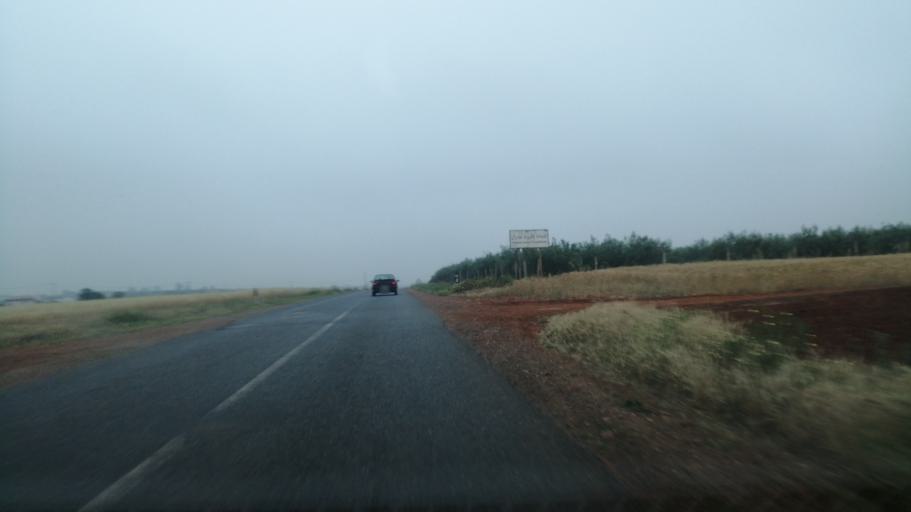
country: MA
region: Rabat-Sale-Zemmour-Zaer
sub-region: Khemisset
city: Tiflet
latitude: 33.7465
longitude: -6.2682
